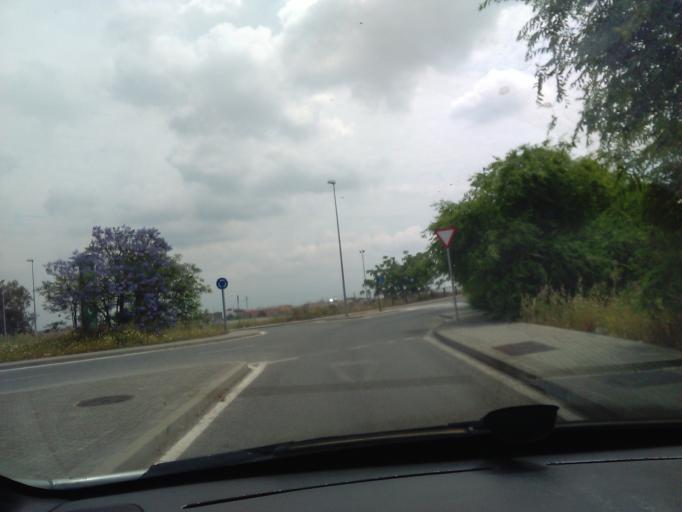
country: ES
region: Andalusia
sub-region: Provincia de Sevilla
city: Sevilla
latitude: 37.3717
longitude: -5.9399
